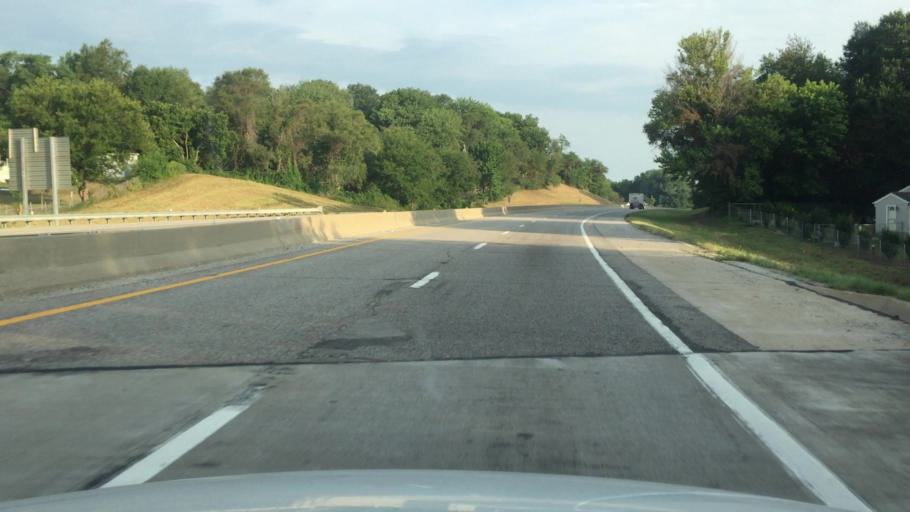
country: US
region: Kansas
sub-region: Doniphan County
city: Elwood
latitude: 39.7278
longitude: -94.8438
